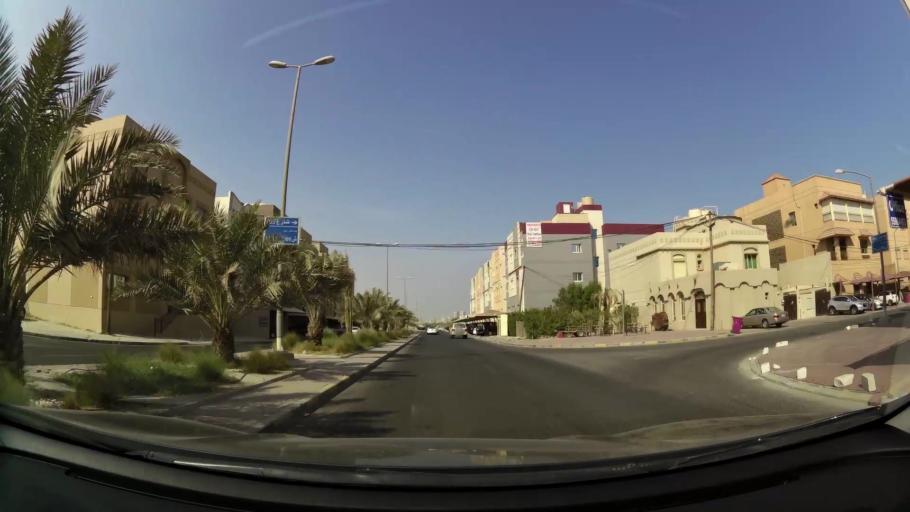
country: KW
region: Al Ahmadi
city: Al Manqaf
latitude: 29.1156
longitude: 48.1225
